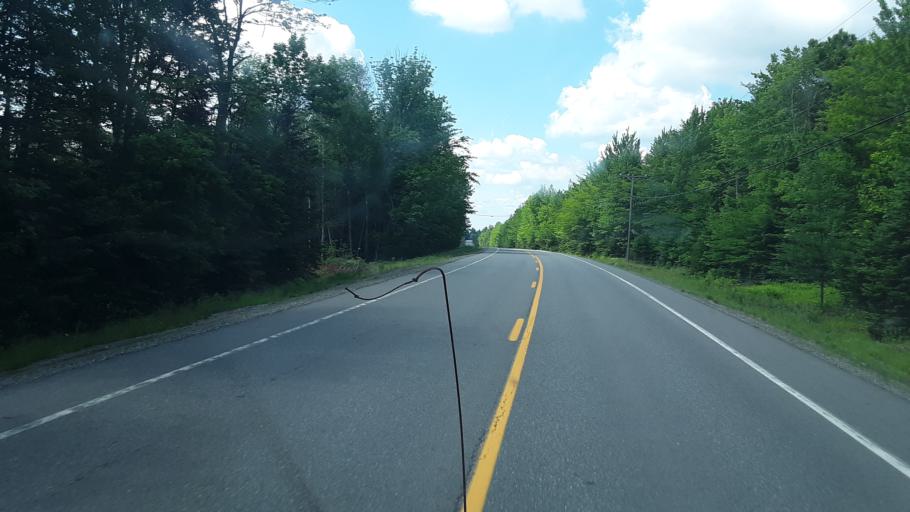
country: US
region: Maine
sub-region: Washington County
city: Machias
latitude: 45.0116
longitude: -67.5546
